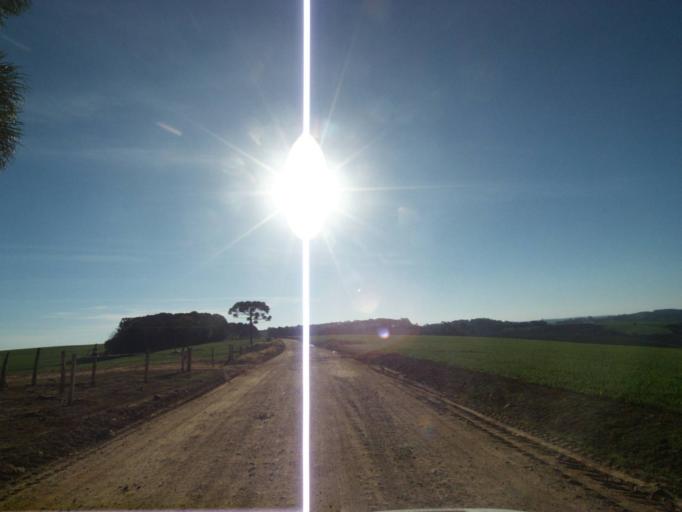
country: BR
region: Parana
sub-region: Telemaco Borba
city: Telemaco Borba
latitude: -24.5217
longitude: -50.6422
